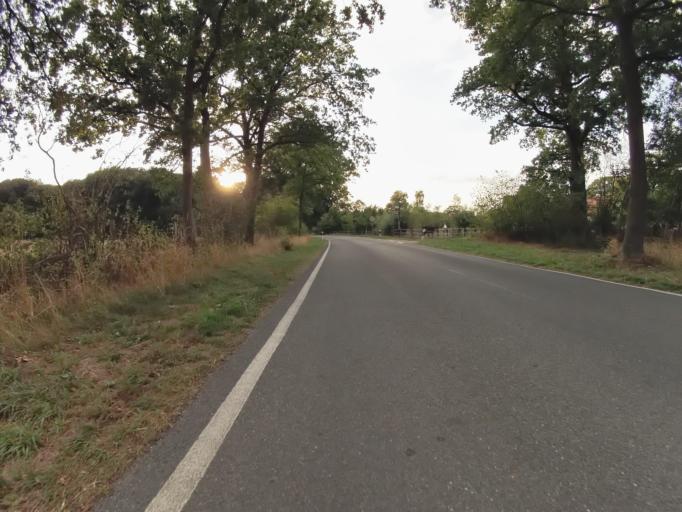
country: DE
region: North Rhine-Westphalia
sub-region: Regierungsbezirk Munster
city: Westerkappeln
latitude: 52.3568
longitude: 7.8972
